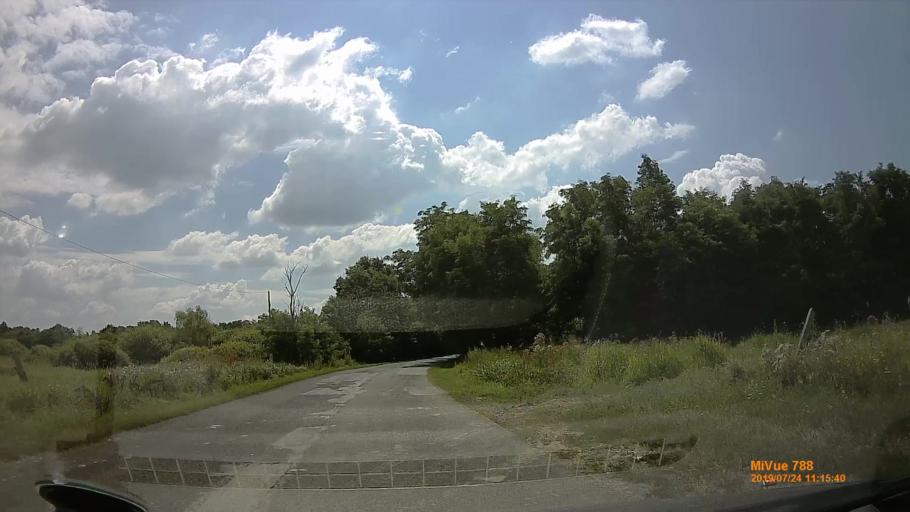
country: HU
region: Szabolcs-Szatmar-Bereg
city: Tarpa
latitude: 48.1888
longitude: 22.4597
